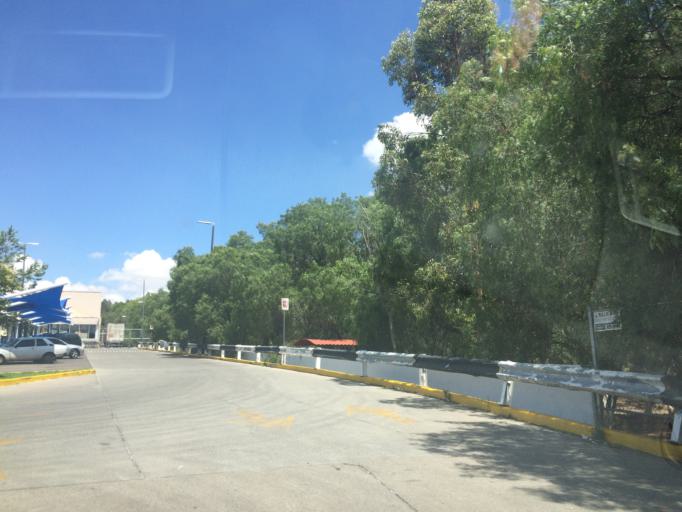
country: MX
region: Zacatecas
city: Zacatecas
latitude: 22.7624
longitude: -102.5494
